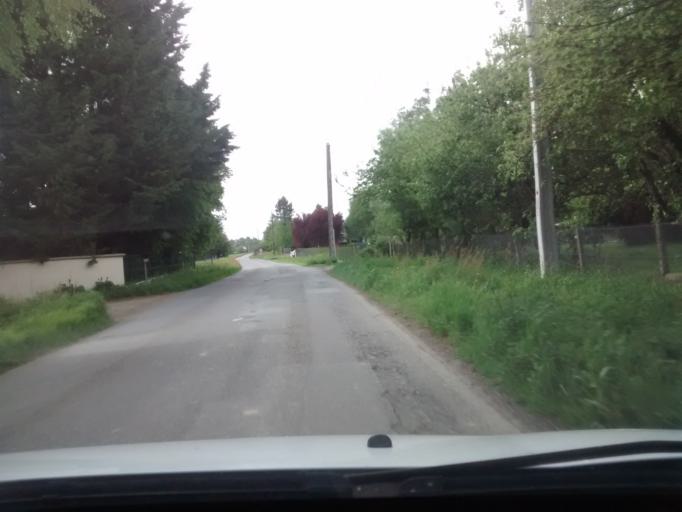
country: FR
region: Brittany
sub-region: Departement d'Ille-et-Vilaine
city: Nouvoitou
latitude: 48.0725
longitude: -1.5426
